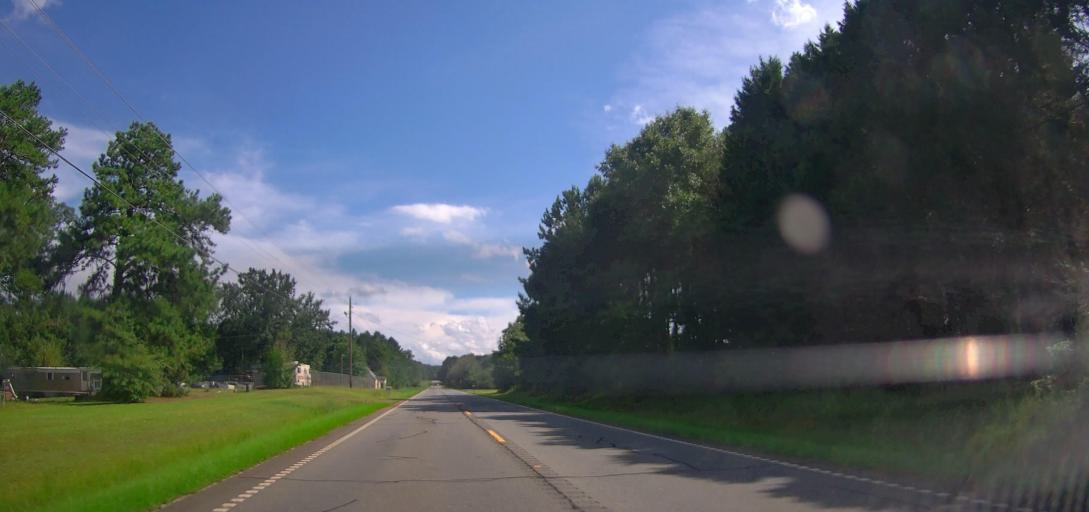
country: US
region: Georgia
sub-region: Meriwether County
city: Manchester
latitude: 32.8318
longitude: -84.6190
